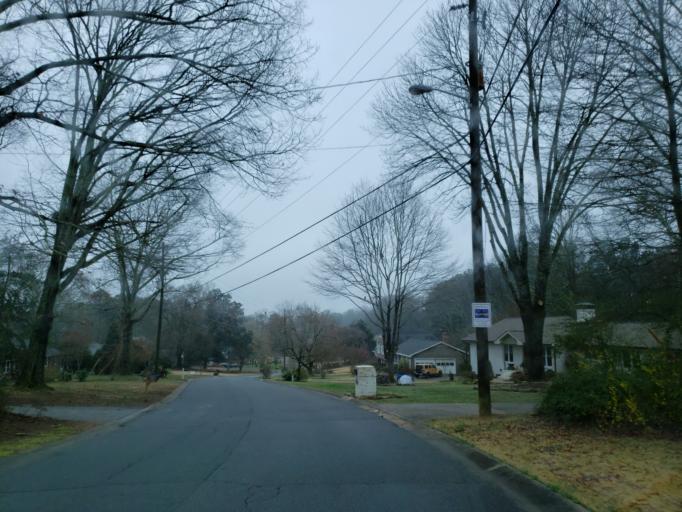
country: US
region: Georgia
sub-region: Cobb County
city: Fair Oaks
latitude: 33.9243
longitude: -84.5699
